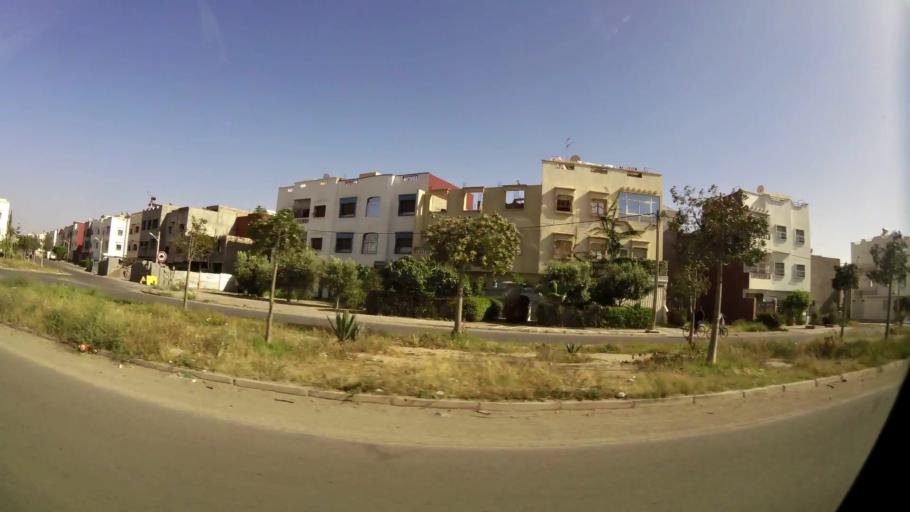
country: MA
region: Souss-Massa-Draa
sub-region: Inezgane-Ait Mellou
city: Inezgane
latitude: 30.3821
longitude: -9.5137
